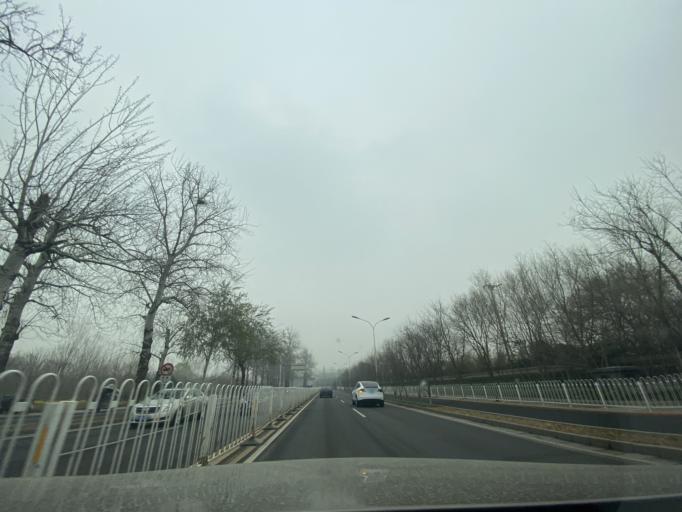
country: CN
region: Beijing
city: Sijiqing
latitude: 39.9711
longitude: 116.2574
